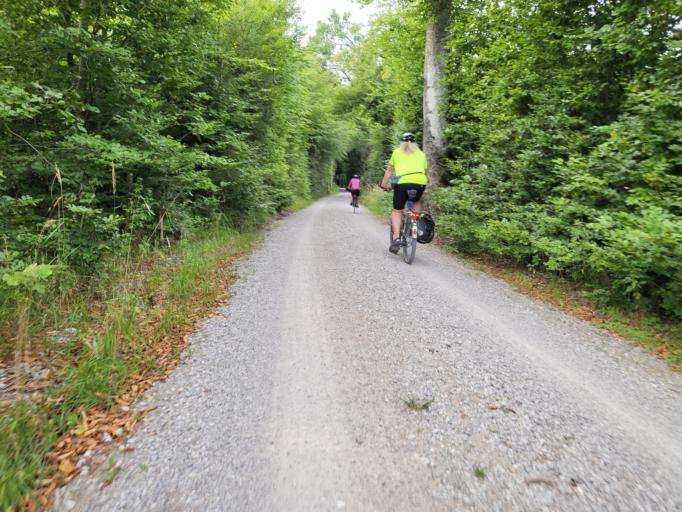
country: DE
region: Bavaria
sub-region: Upper Bavaria
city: Aying
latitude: 47.9877
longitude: 11.7634
